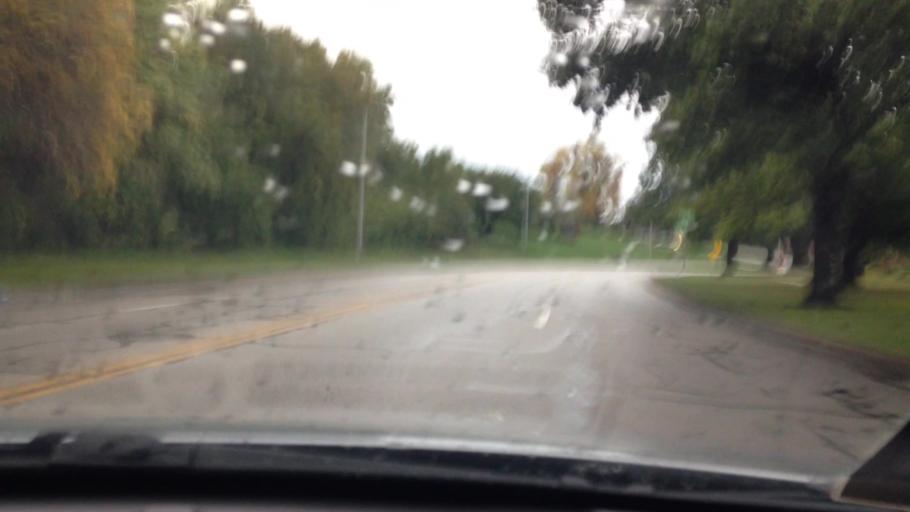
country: US
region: Kansas
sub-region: Johnson County
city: Mission Hills
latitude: 39.0120
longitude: -94.5709
